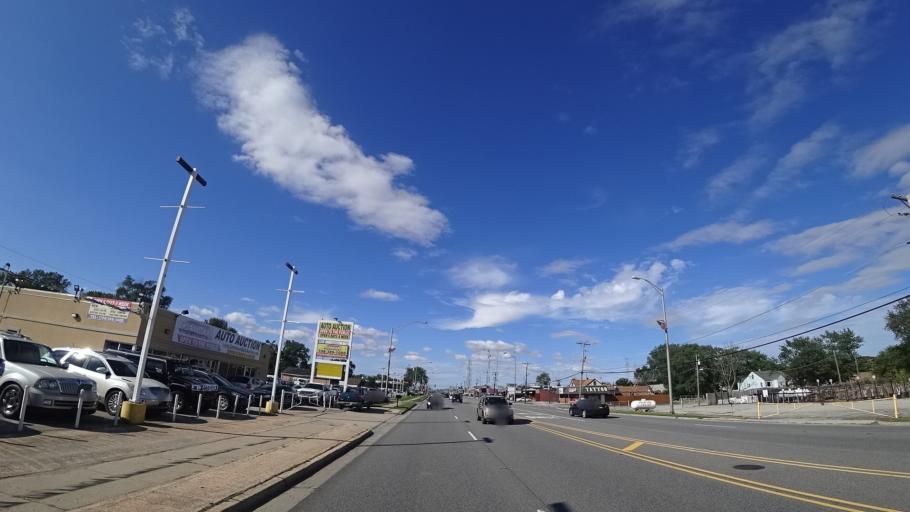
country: US
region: Illinois
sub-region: Cook County
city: Midlothian
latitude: 41.6358
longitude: -87.7378
